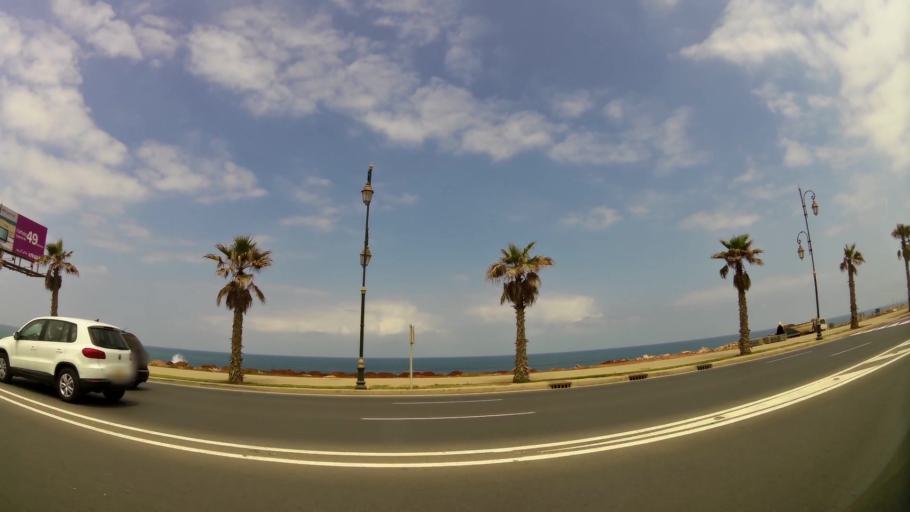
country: MA
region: Rabat-Sale-Zemmour-Zaer
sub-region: Skhirate-Temara
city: Temara
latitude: 33.9846
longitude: -6.8915
